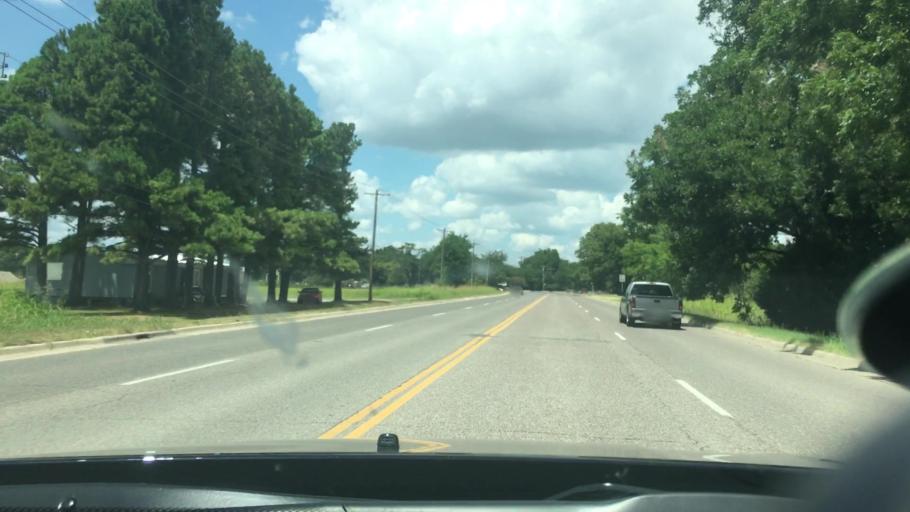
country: US
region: Oklahoma
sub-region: Murray County
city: Davis
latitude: 34.4717
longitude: -97.1316
